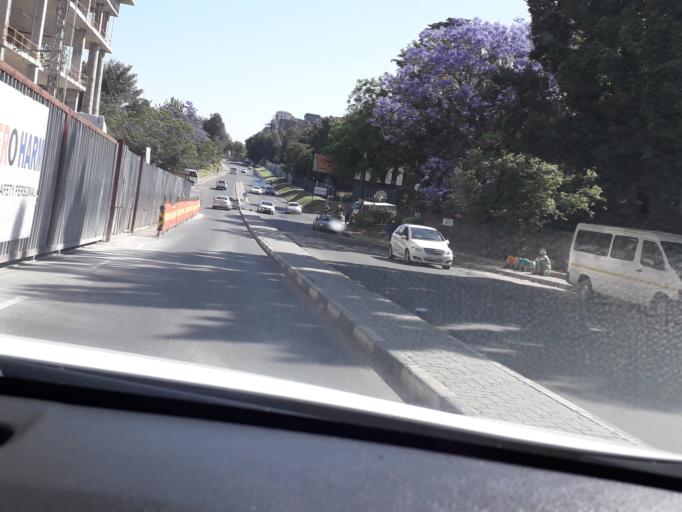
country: ZA
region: Gauteng
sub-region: City of Johannesburg Metropolitan Municipality
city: Johannesburg
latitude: -26.0984
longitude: 28.0506
